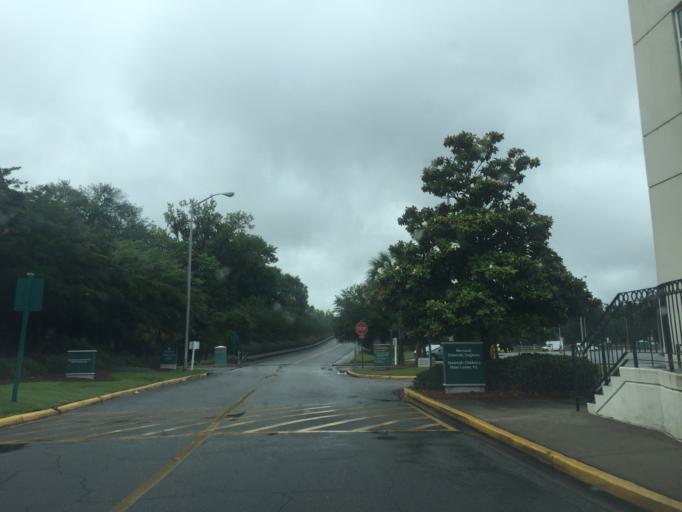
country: US
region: Georgia
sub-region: Chatham County
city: Thunderbolt
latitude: 32.0312
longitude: -81.0873
